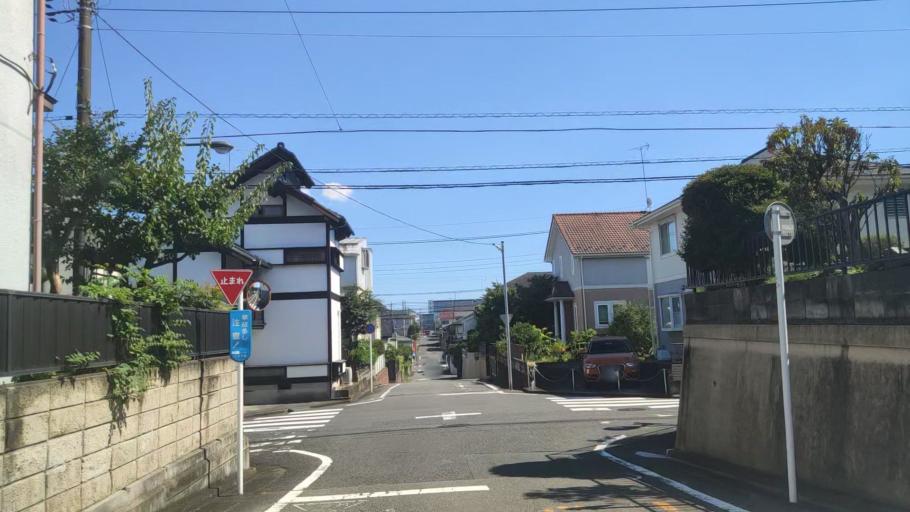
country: JP
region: Tokyo
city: Hachioji
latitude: 35.6471
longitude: 139.3068
